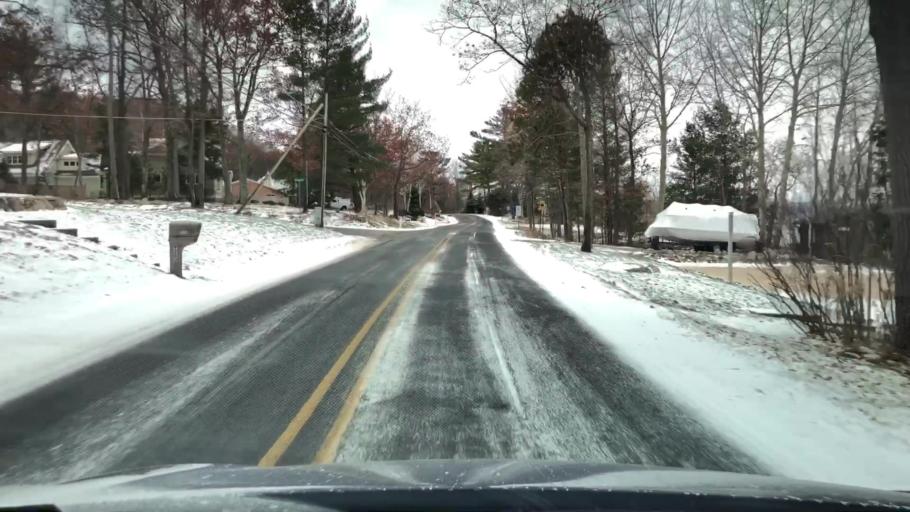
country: US
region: Michigan
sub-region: Grand Traverse County
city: Traverse City
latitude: 44.8216
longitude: -85.5725
